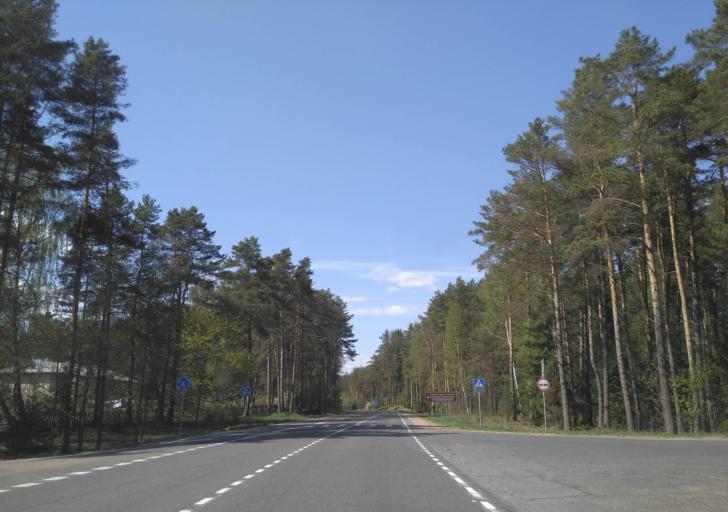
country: BY
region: Minsk
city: Narach
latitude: 54.9134
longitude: 26.7222
